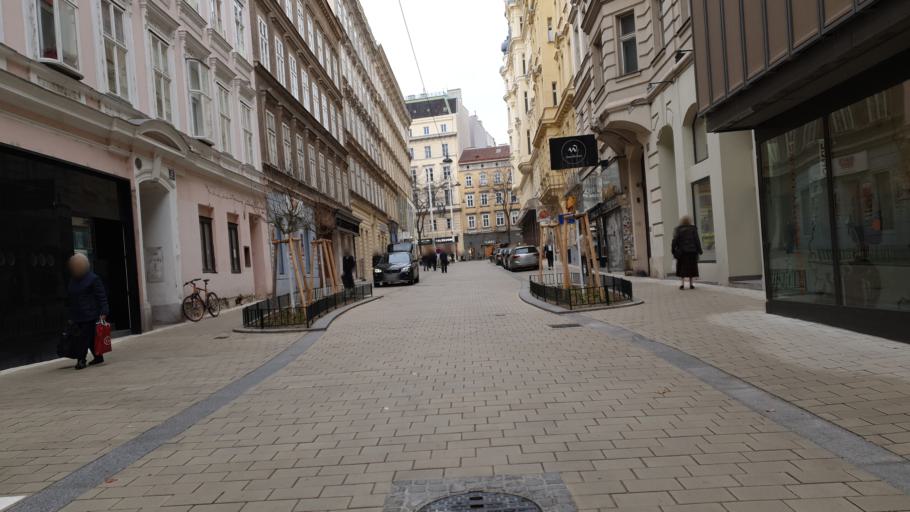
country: AT
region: Vienna
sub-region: Wien Stadt
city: Vienna
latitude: 48.1965
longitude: 16.3482
